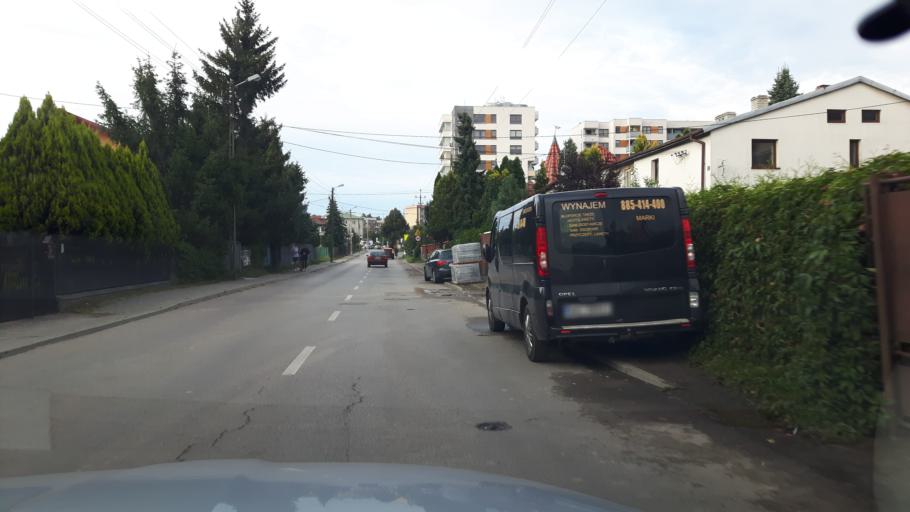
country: PL
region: Masovian Voivodeship
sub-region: Powiat wolominski
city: Marki
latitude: 52.3268
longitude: 21.1003
